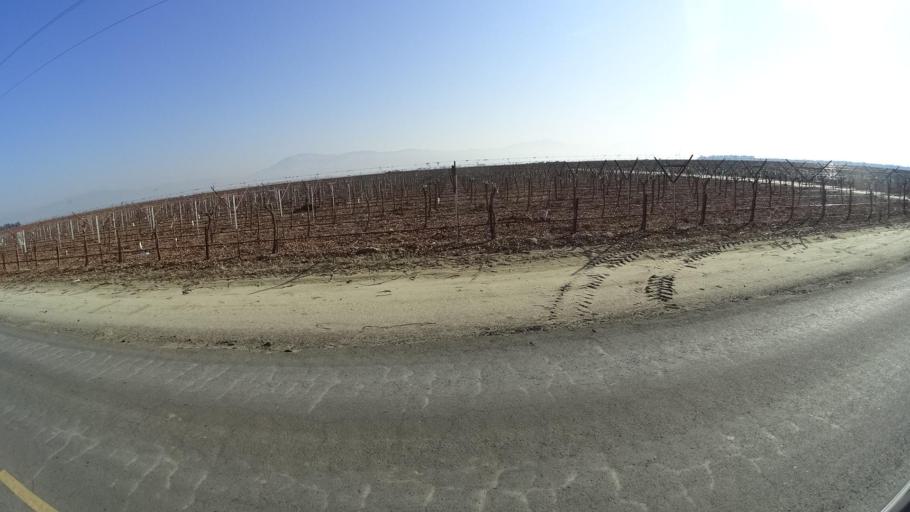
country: US
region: California
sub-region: Kern County
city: Weedpatch
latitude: 35.1172
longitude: -118.9677
